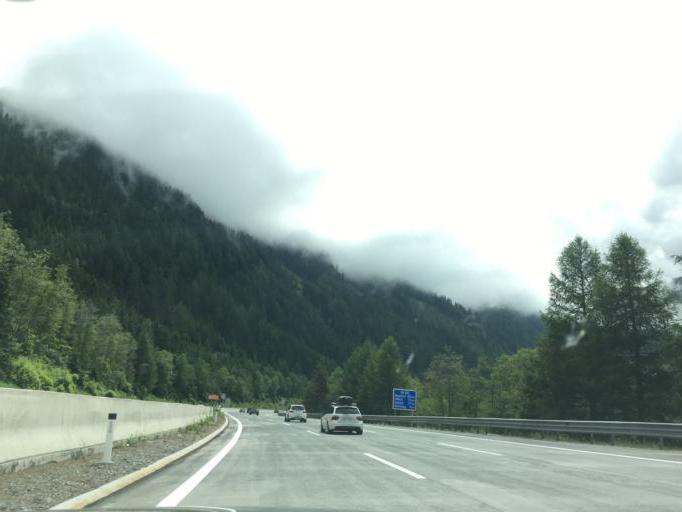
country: AT
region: Salzburg
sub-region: Politischer Bezirk Tamsweg
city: Sankt Michael im Lungau
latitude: 47.0879
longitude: 13.6068
